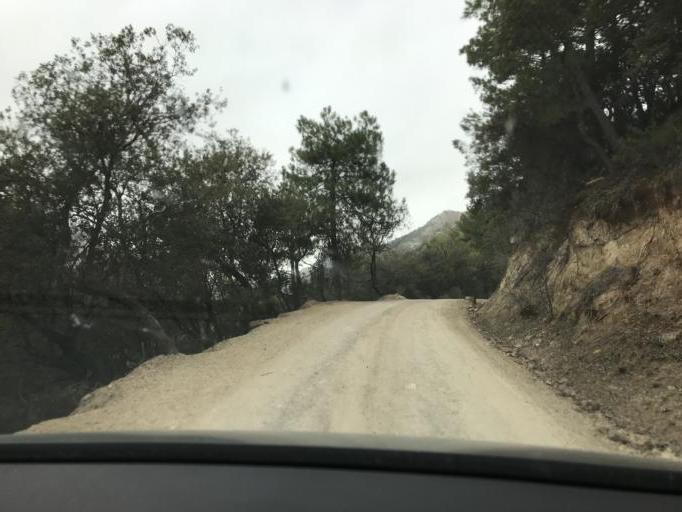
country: ES
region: Andalusia
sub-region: Provincia de Granada
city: Castril
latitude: 37.8792
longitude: -2.7558
